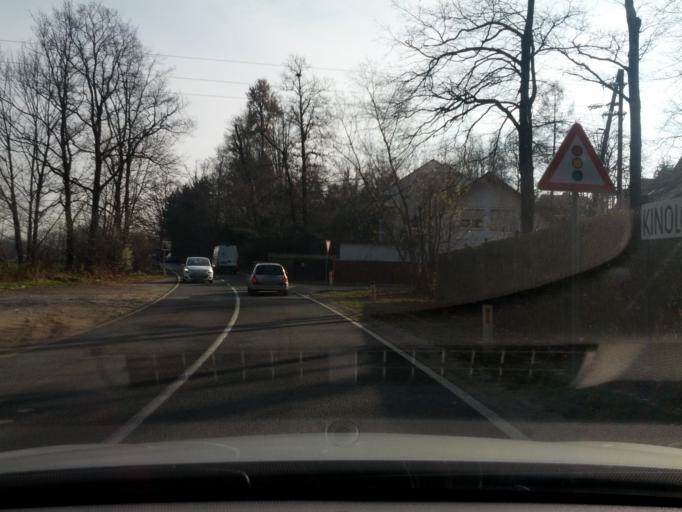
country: SI
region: Ljubljana
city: Ljubljana
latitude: 46.0520
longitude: 14.4565
